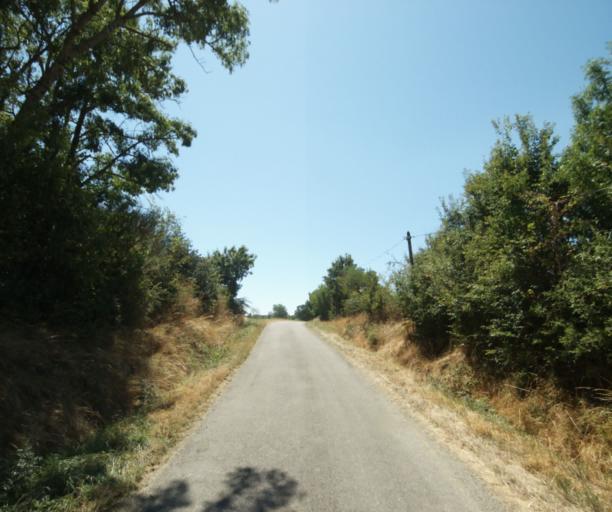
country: FR
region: Midi-Pyrenees
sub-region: Departement de la Haute-Garonne
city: Saint-Felix-Lauragais
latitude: 43.4564
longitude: 1.8988
